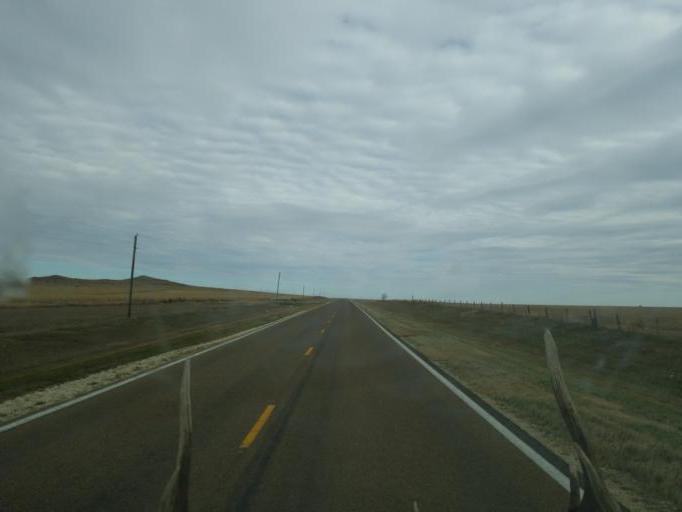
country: US
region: Kansas
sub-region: Wallace County
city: Sharon Springs
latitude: 39.0052
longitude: -101.3821
